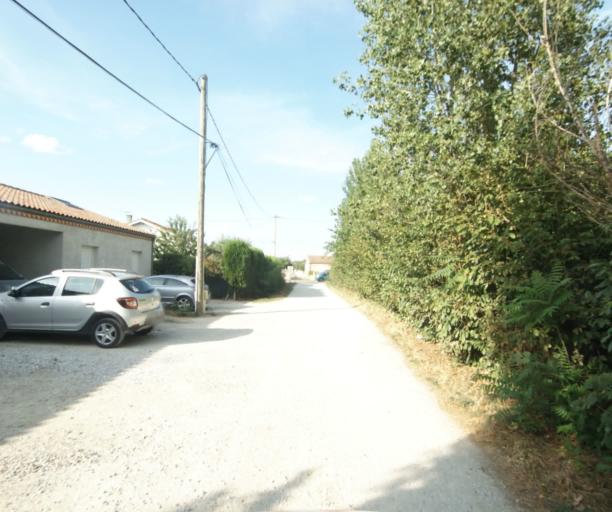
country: FR
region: Midi-Pyrenees
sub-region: Departement de la Haute-Garonne
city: Revel
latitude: 43.4634
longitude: 1.9910
